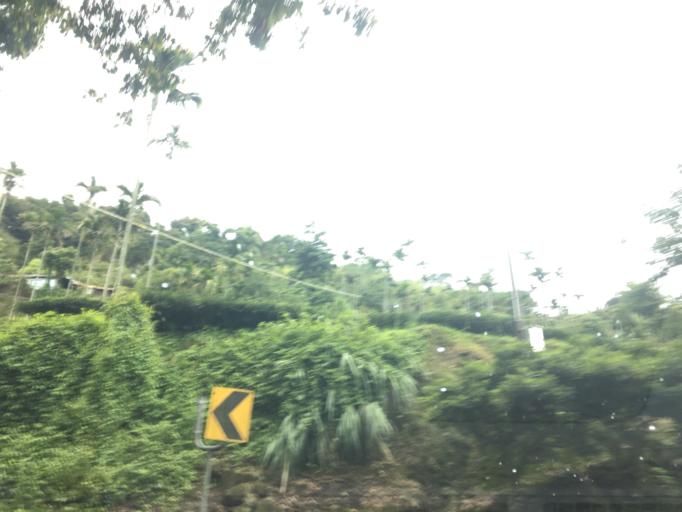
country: TW
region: Taiwan
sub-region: Yunlin
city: Douliu
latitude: 23.5529
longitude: 120.6714
